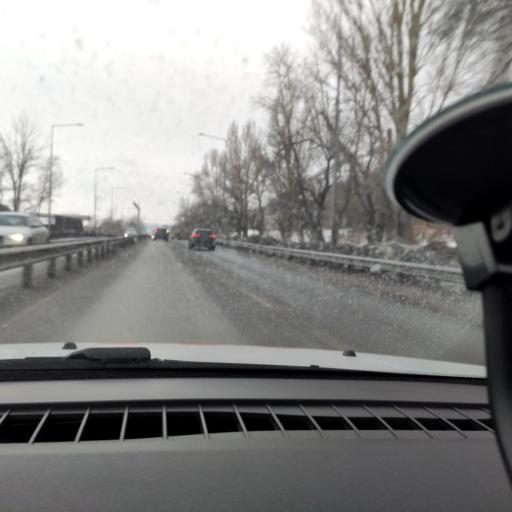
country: RU
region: Samara
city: Volzhskiy
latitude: 53.3971
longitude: 50.1525
